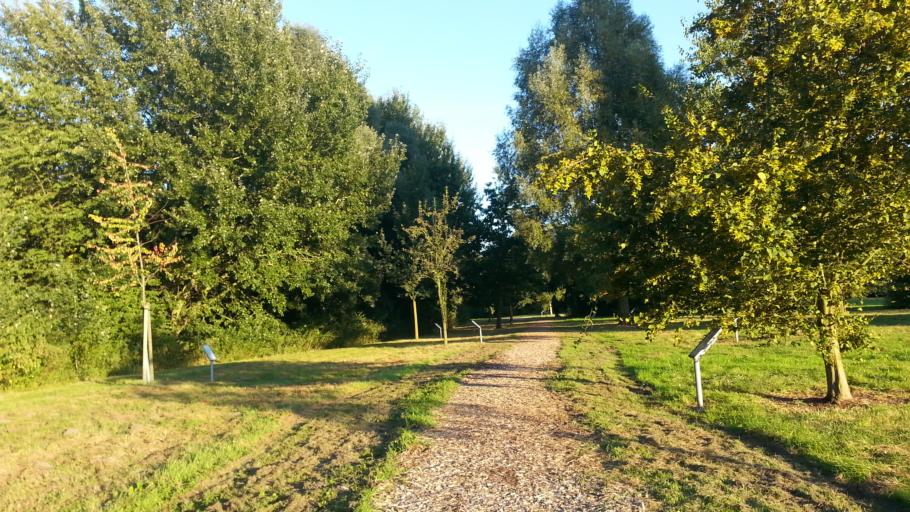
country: DE
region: North Rhine-Westphalia
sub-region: Regierungsbezirk Munster
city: Muenster
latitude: 51.9503
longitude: 7.5949
